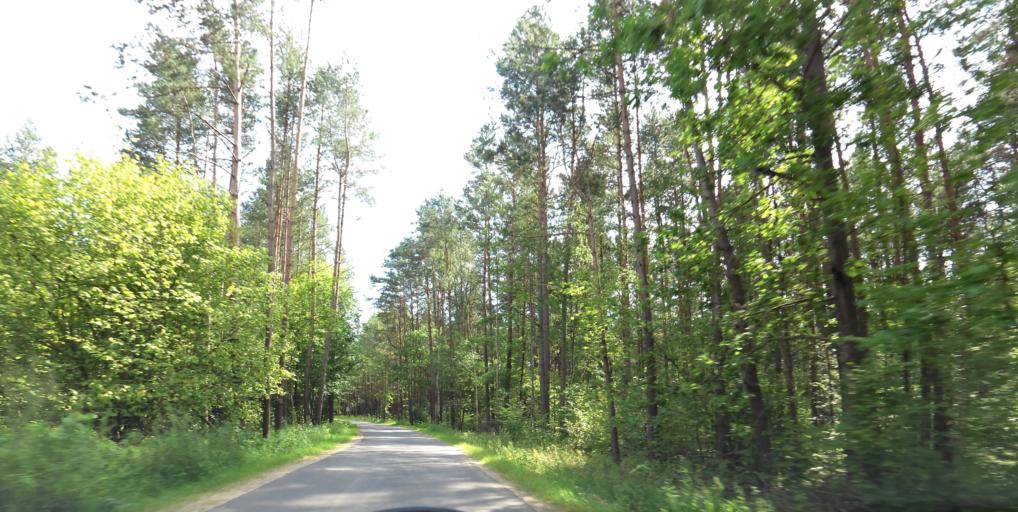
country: LT
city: Grigiskes
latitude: 54.7261
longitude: 25.0479
